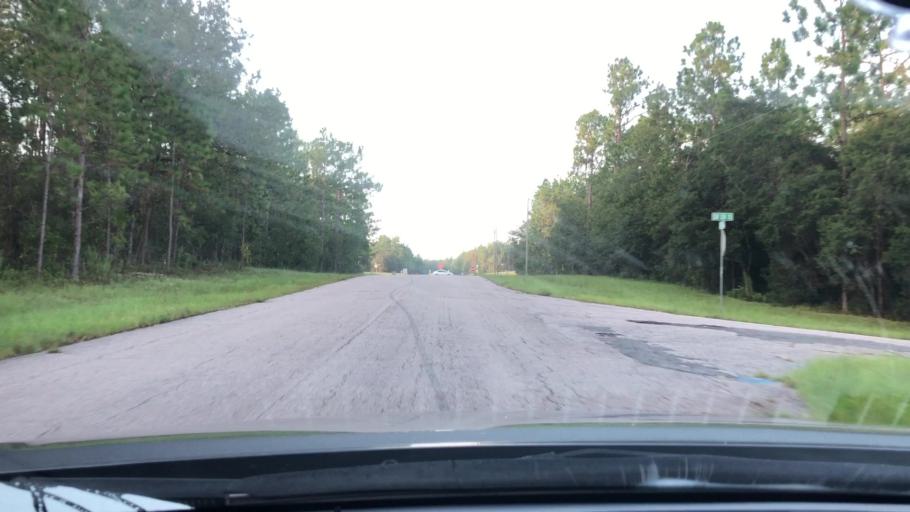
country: US
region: Florida
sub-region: Marion County
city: Belleview
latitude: 29.0280
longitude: -82.2403
